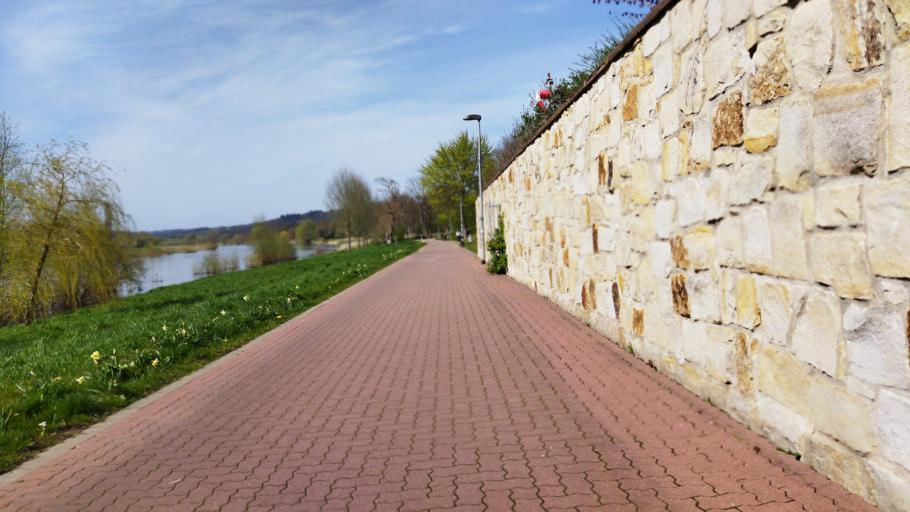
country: DE
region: Lower Saxony
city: Hameln
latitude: 52.1078
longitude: 9.3509
